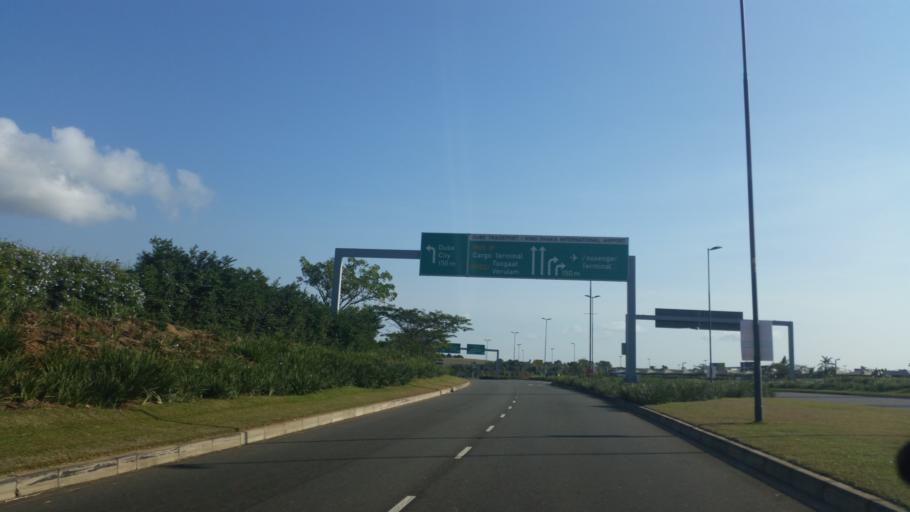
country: ZA
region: KwaZulu-Natal
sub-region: iLembe District Municipality
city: Ballitoville
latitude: -29.6237
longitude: 31.1008
